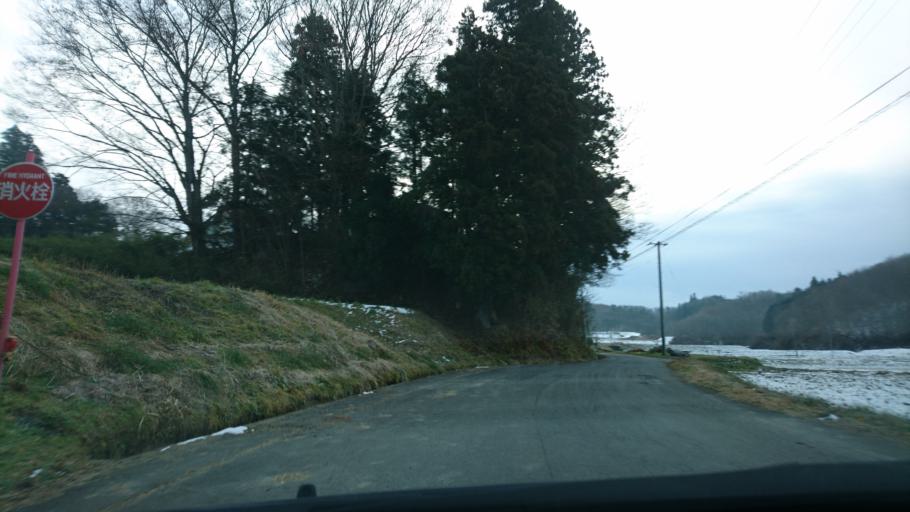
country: JP
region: Iwate
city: Ichinoseki
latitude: 38.9064
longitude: 141.3437
